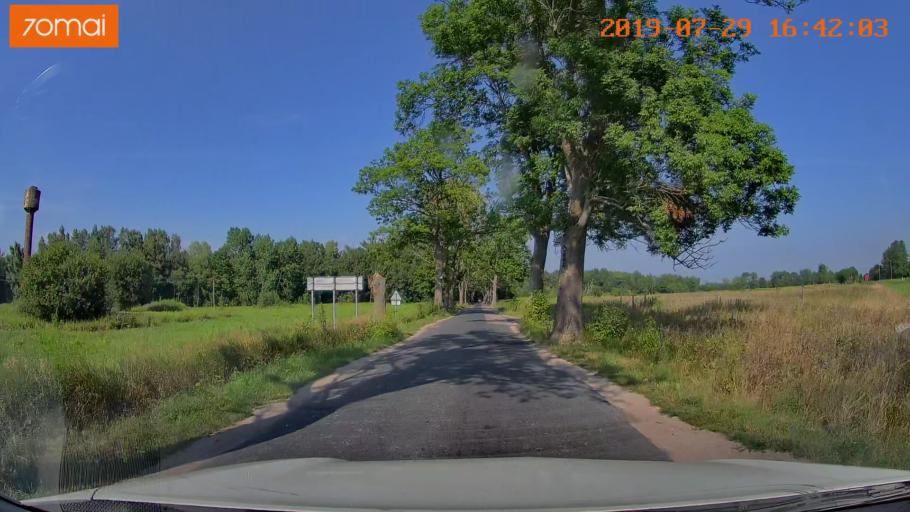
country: RU
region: Kaliningrad
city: Primorsk
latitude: 54.7404
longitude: 20.0688
